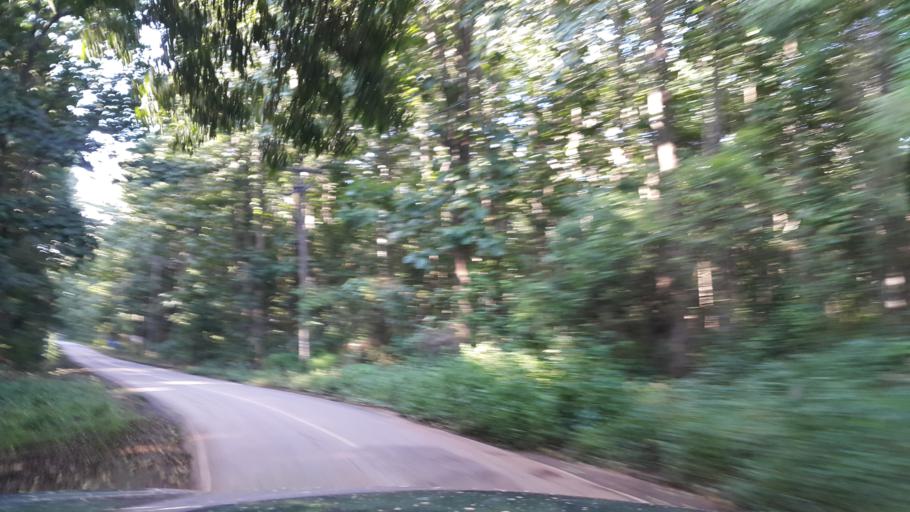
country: TH
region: Chiang Mai
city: Mae Taeng
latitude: 19.0700
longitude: 99.0823
